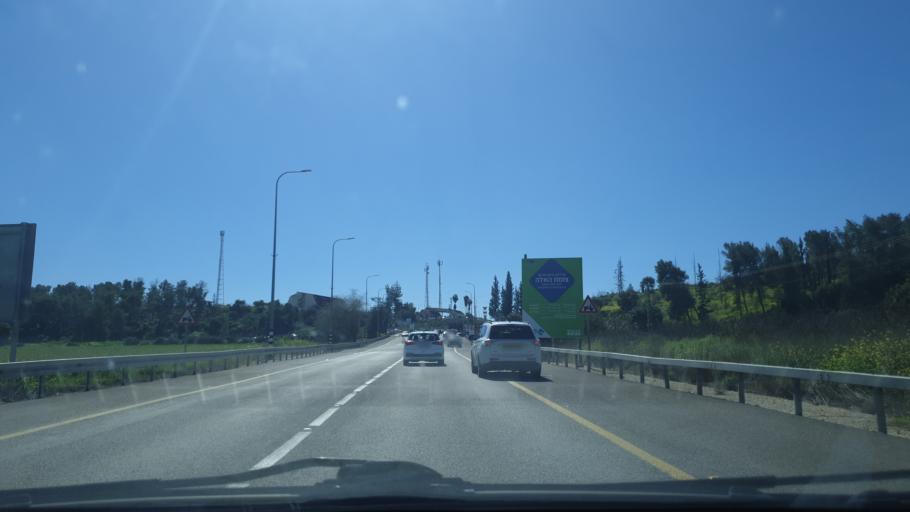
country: IL
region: Jerusalem
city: Bet Shemesh
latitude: 31.6893
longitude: 34.9453
